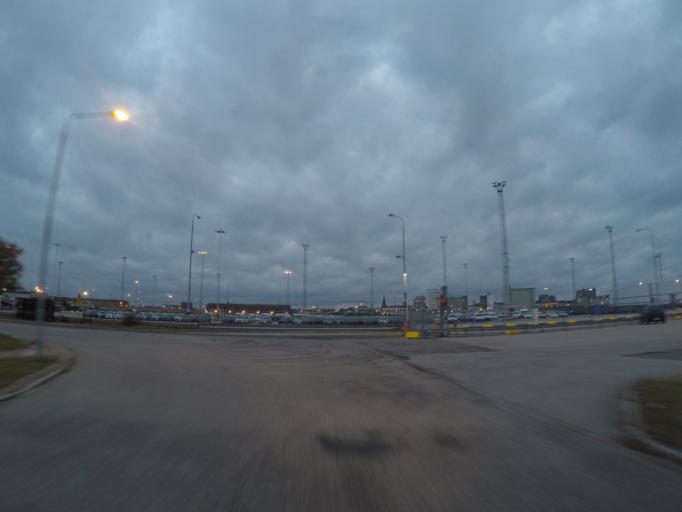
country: SE
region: Skane
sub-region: Malmo
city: Malmoe
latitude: 55.6206
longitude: 13.0045
